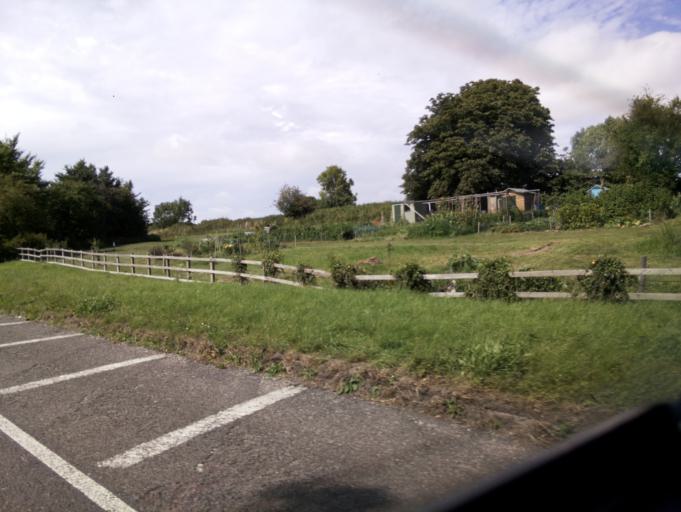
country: GB
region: England
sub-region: Dorset
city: Dorchester
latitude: 50.7409
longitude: -2.4885
